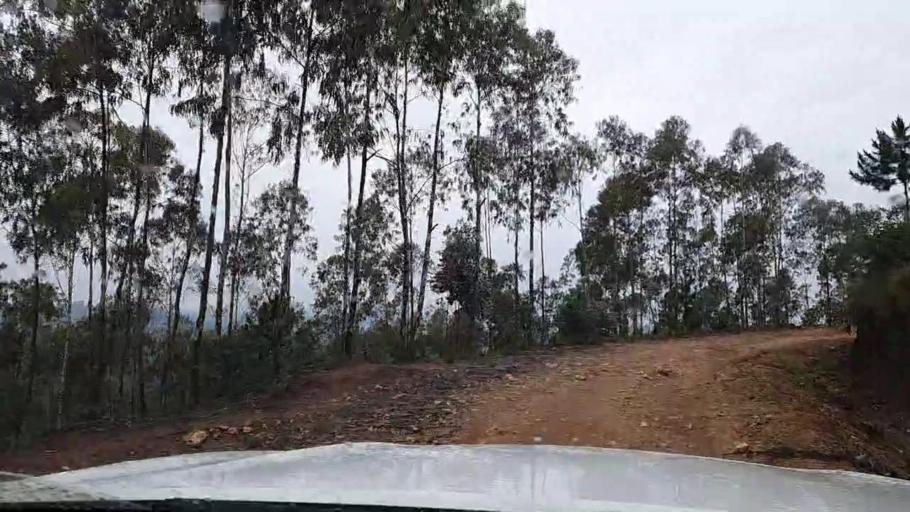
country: RW
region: Southern Province
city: Nzega
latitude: -2.4696
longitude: 29.4977
